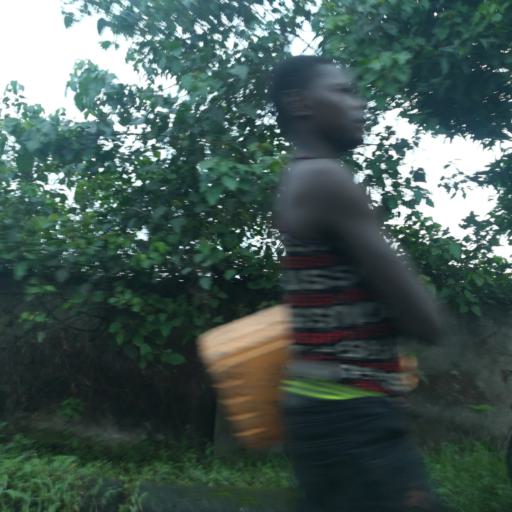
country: NG
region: Rivers
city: Port Harcourt
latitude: 4.7581
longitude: 7.0112
